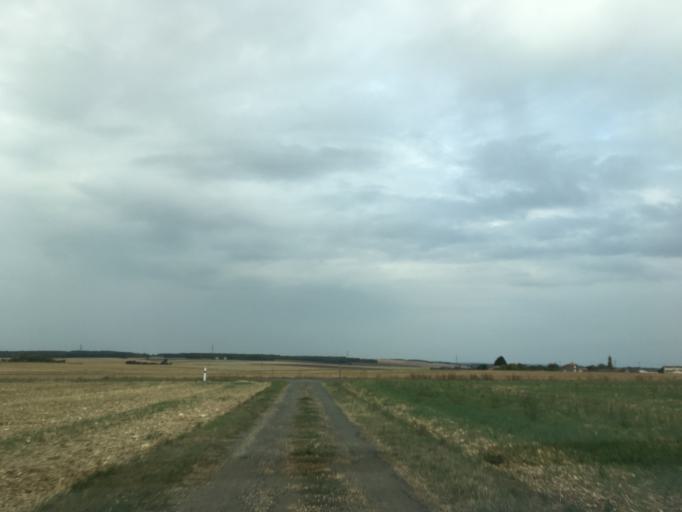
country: FR
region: Poitou-Charentes
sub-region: Departement des Deux-Sevres
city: Beauvoir-sur-Niort
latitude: 46.0824
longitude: -0.4998
